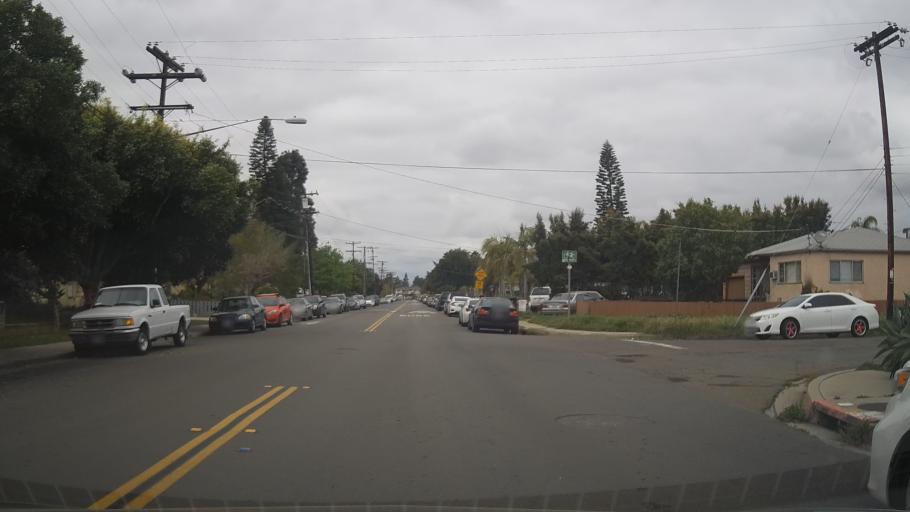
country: US
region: California
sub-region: San Diego County
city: La Mesa
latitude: 32.7677
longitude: -117.0490
